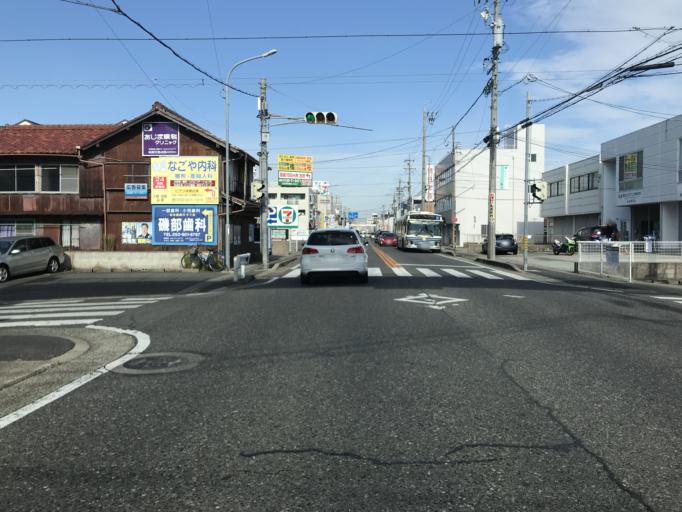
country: JP
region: Aichi
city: Nagoya-shi
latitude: 35.2189
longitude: 136.9334
